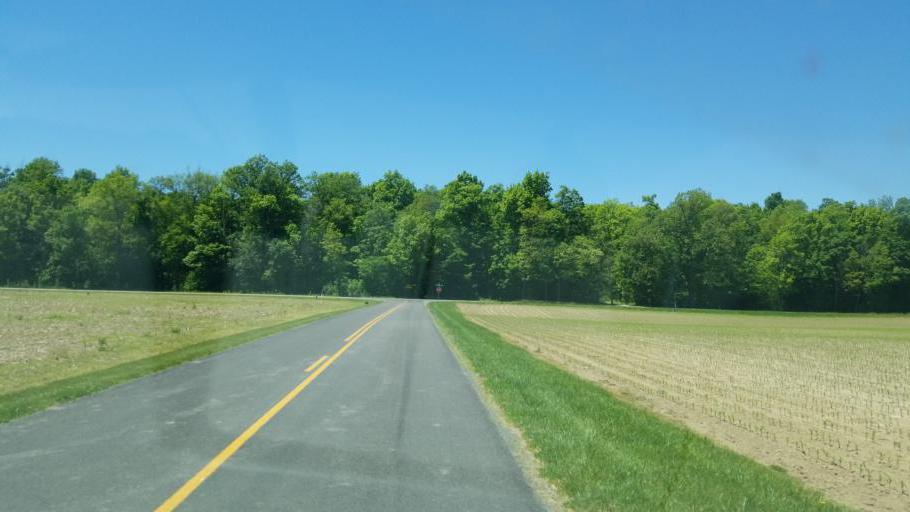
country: US
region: Ohio
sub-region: Mercer County
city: Fort Recovery
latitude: 40.3673
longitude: -84.8025
